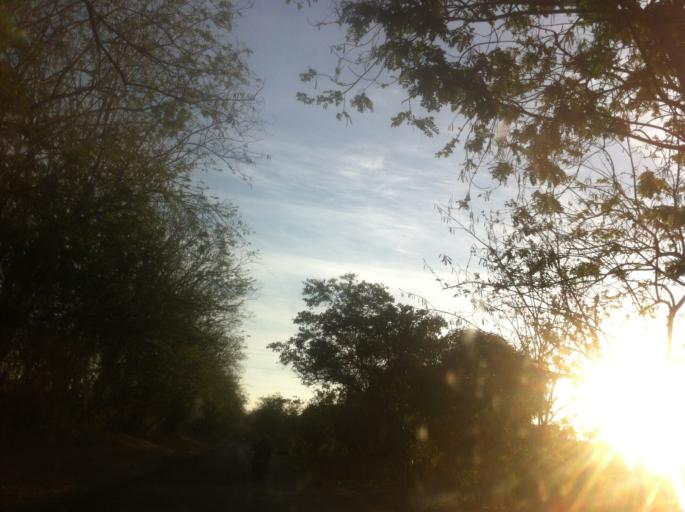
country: NI
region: Rivas
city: Potosi
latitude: 11.4945
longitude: -85.8682
